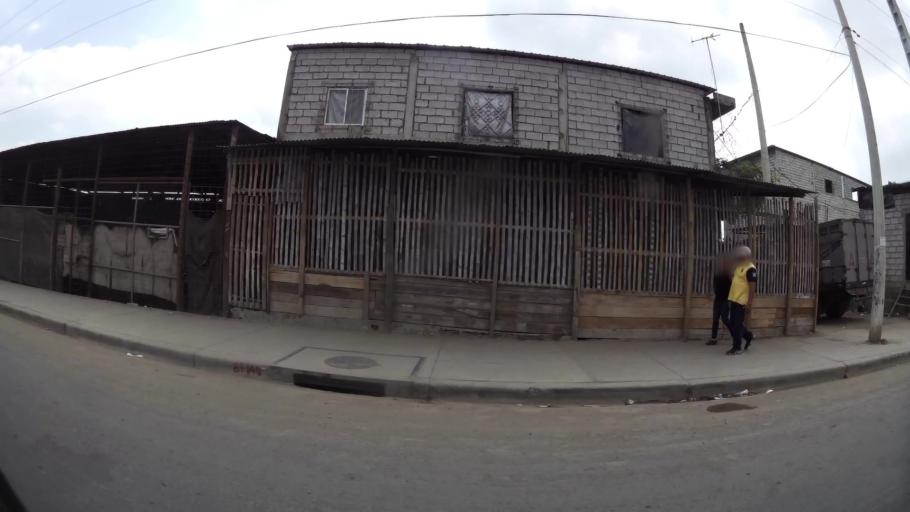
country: EC
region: Guayas
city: Santa Lucia
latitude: -2.1170
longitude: -79.9486
